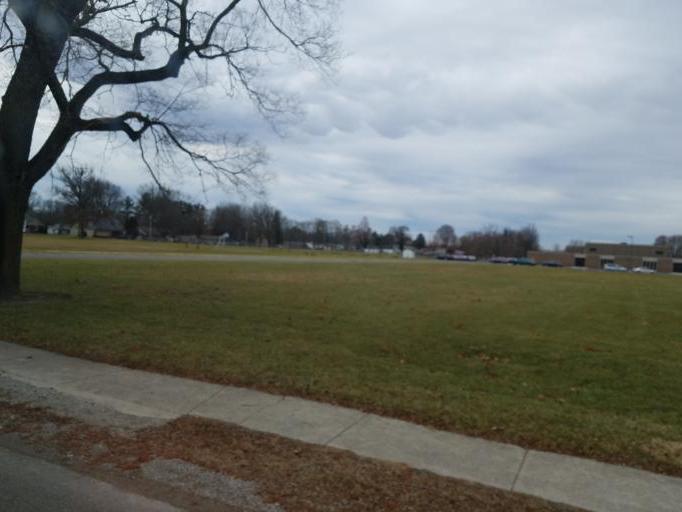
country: US
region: Ohio
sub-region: Marion County
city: Marion
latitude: 40.5855
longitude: -83.1040
